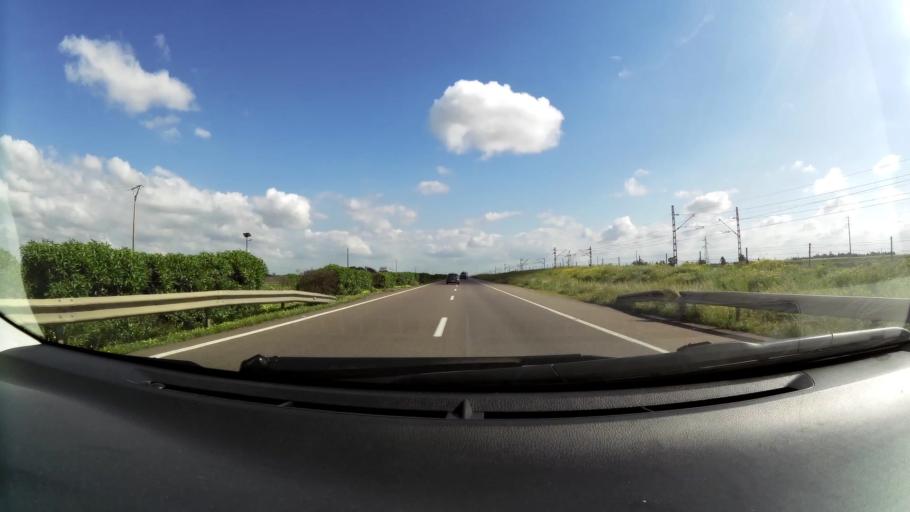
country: MA
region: Chaouia-Ouardigha
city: Nouaseur
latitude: 33.3551
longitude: -7.6175
